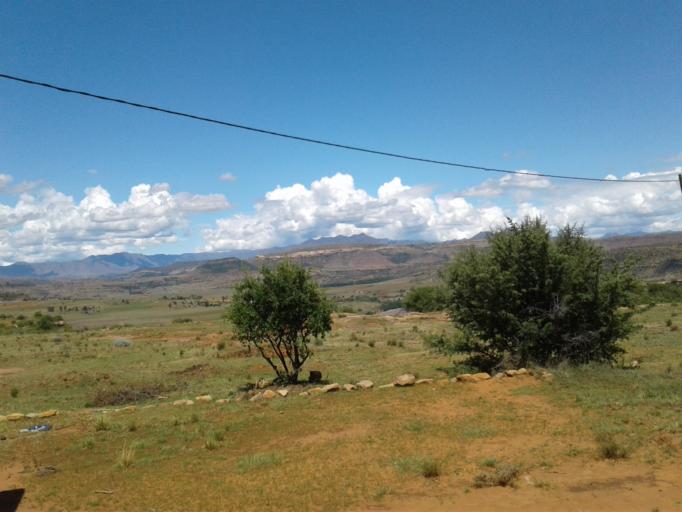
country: LS
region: Quthing
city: Quthing
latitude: -30.3778
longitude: 27.5567
